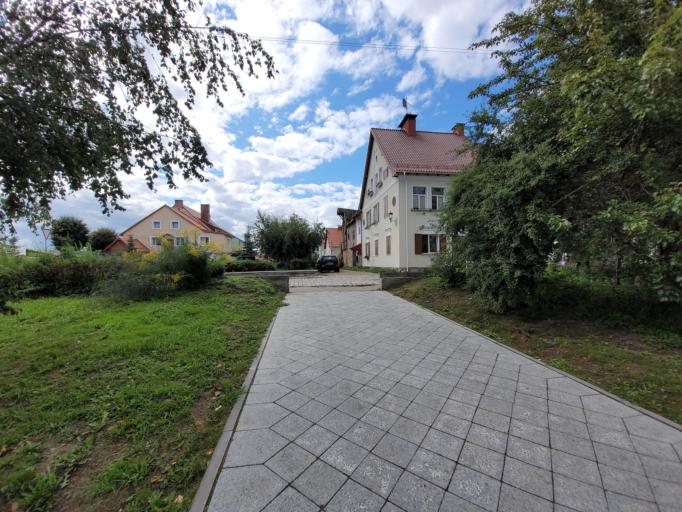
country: RU
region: Kaliningrad
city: Zheleznodorozhnyy
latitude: 54.3616
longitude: 21.3059
